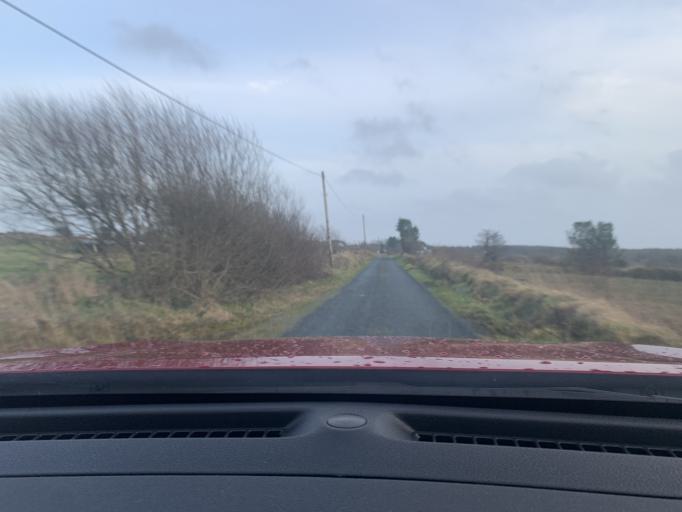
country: IE
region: Connaught
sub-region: Roscommon
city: Ballaghaderreen
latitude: 53.9561
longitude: -8.5315
